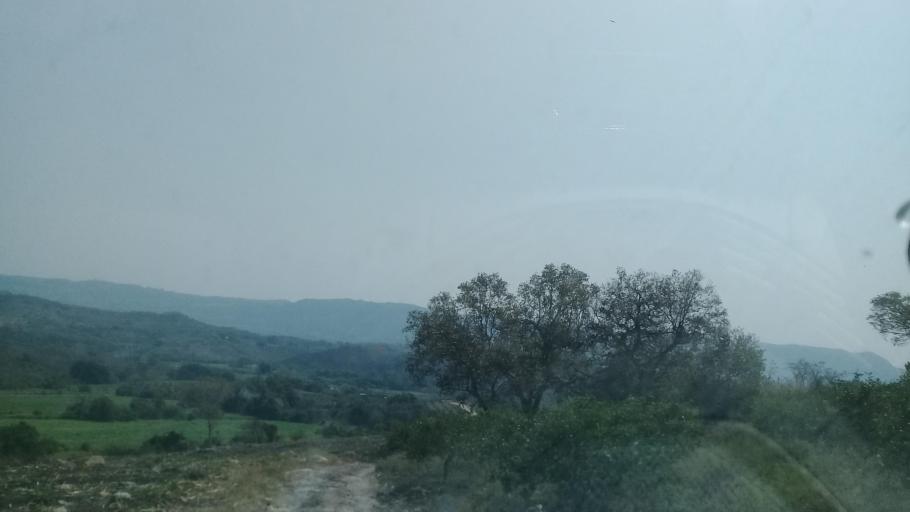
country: MX
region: Veracruz
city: El Castillo
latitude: 19.5705
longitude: -96.8060
